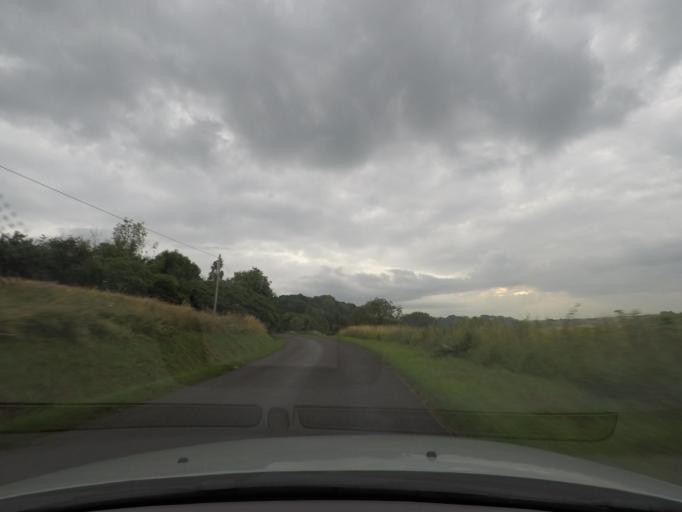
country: FR
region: Haute-Normandie
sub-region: Departement de la Seine-Maritime
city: Neufchatel-en-Bray
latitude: 49.7324
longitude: 1.4657
